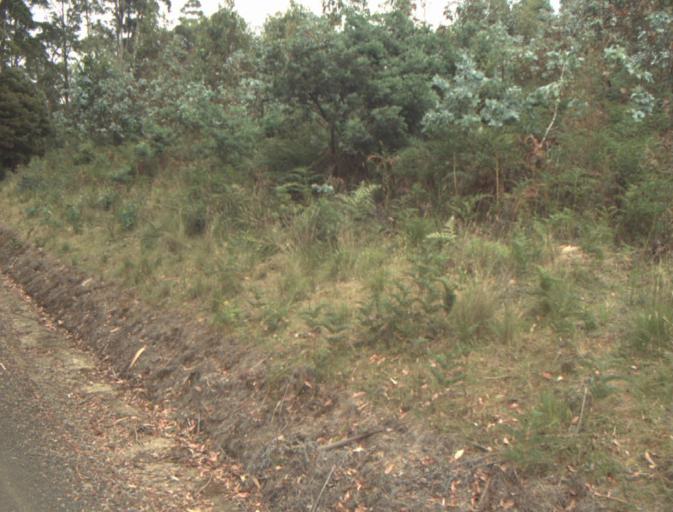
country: AU
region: Tasmania
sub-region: Northern Midlands
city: Evandale
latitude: -41.4538
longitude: 147.4763
